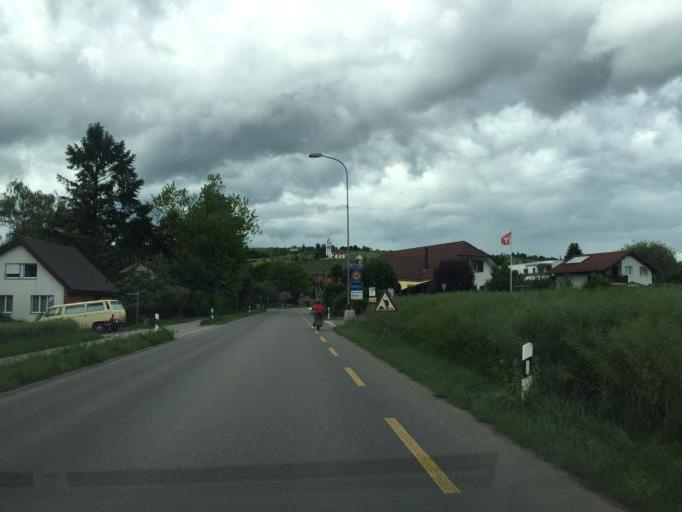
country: CH
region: Schaffhausen
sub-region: Bezirk Unterklettgau
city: Hallau
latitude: 47.6945
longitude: 8.4658
